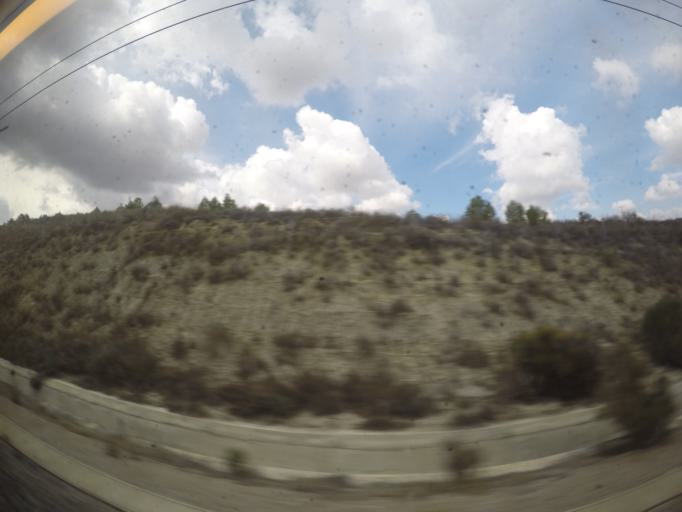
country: ES
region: Catalonia
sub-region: Provincia de Barcelona
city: Sant Llorenc d'Hortons
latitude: 41.4445
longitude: 1.8346
